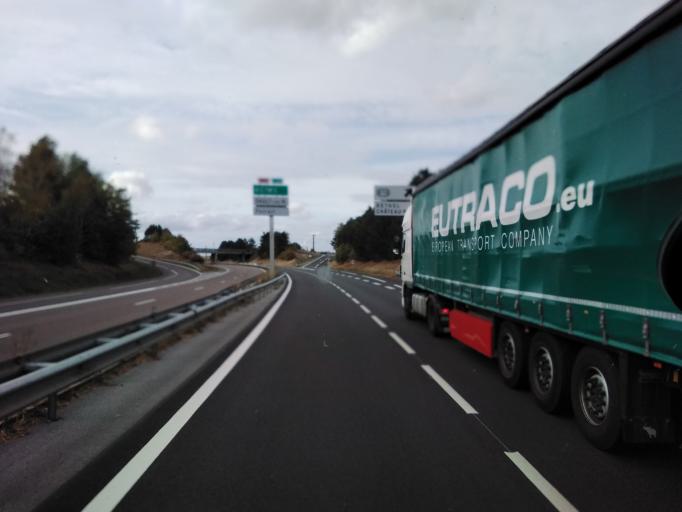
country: FR
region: Champagne-Ardenne
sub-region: Departement des Ardennes
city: Rethel
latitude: 49.5224
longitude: 4.3751
